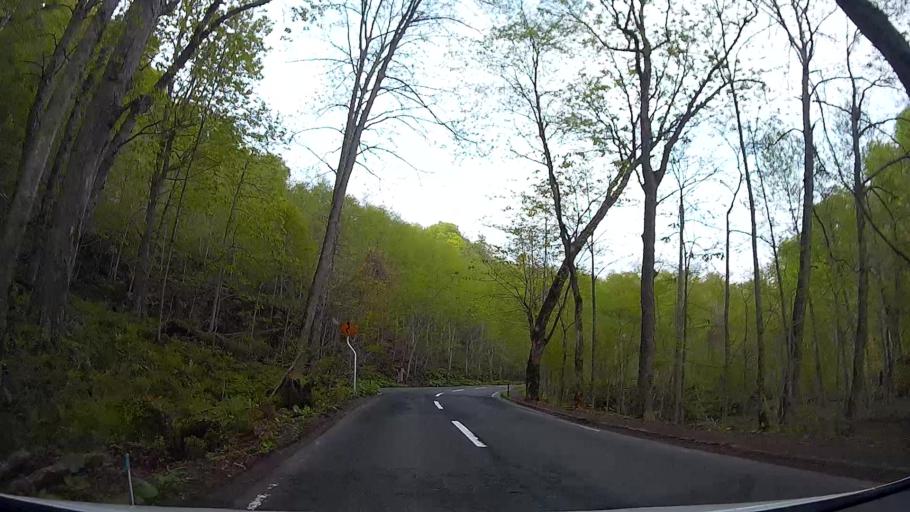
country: JP
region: Aomori
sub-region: Aomori Shi
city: Furudate
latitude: 40.5275
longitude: 140.9740
